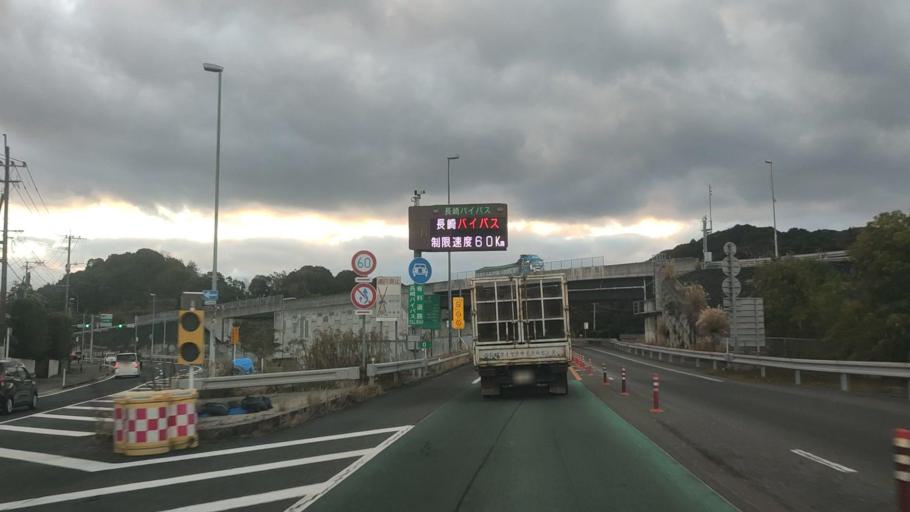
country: JP
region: Nagasaki
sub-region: Isahaya-shi
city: Isahaya
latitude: 32.8171
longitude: 129.9670
